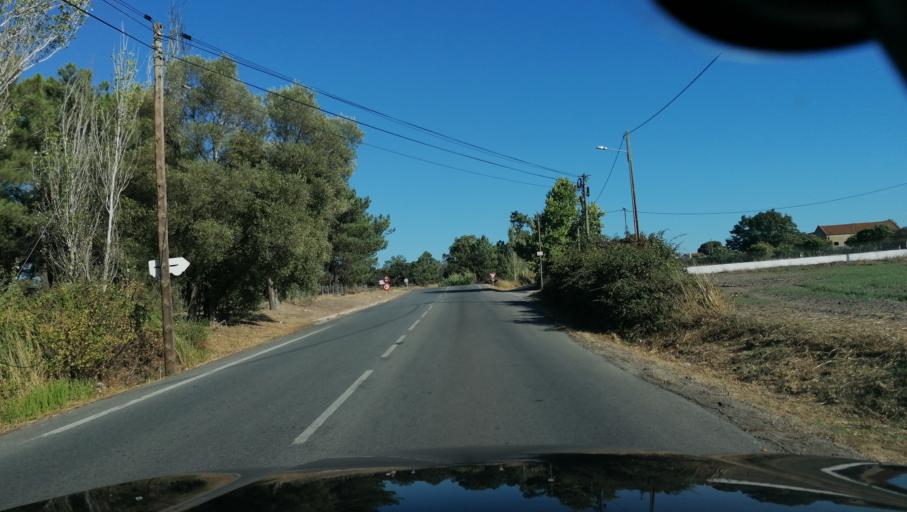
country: PT
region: Setubal
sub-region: Moita
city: Moita
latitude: 38.6360
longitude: -8.9726
